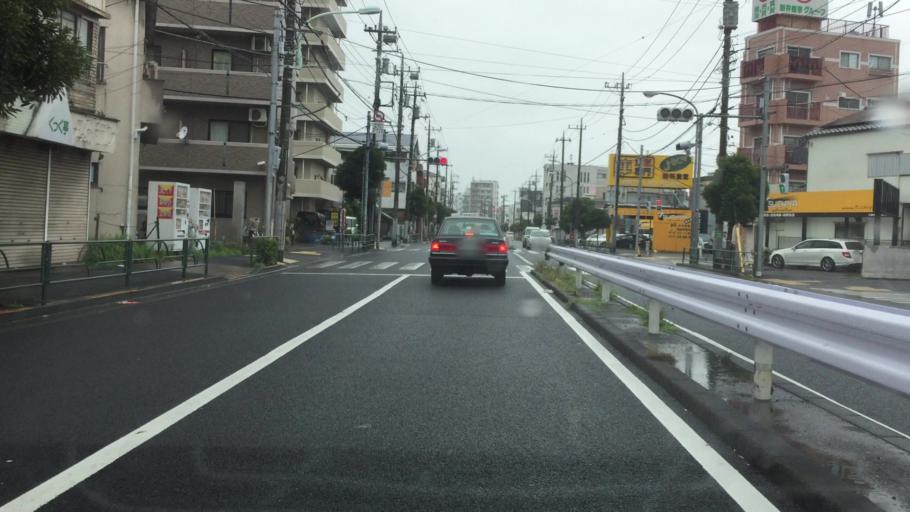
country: JP
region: Saitama
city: Soka
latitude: 35.7668
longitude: 139.7862
